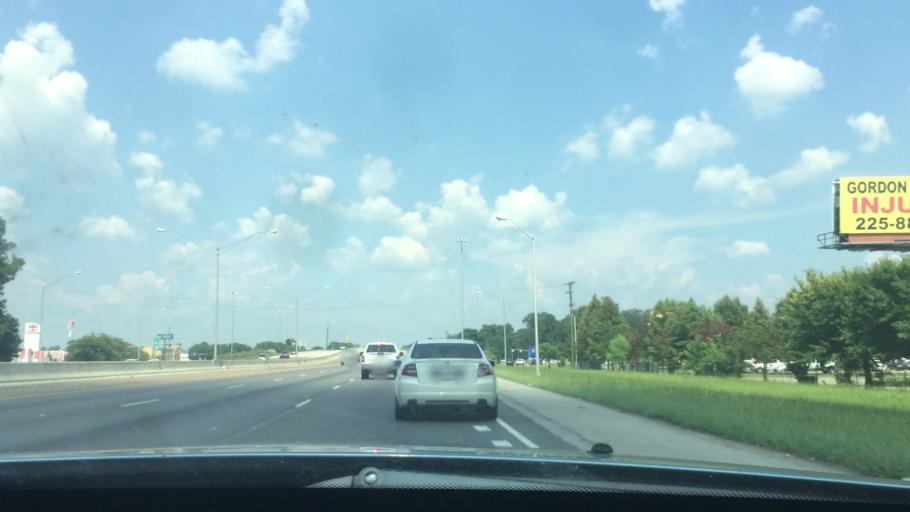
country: US
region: Louisiana
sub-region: East Baton Rouge Parish
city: Shenandoah
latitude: 30.4411
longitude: -91.0122
